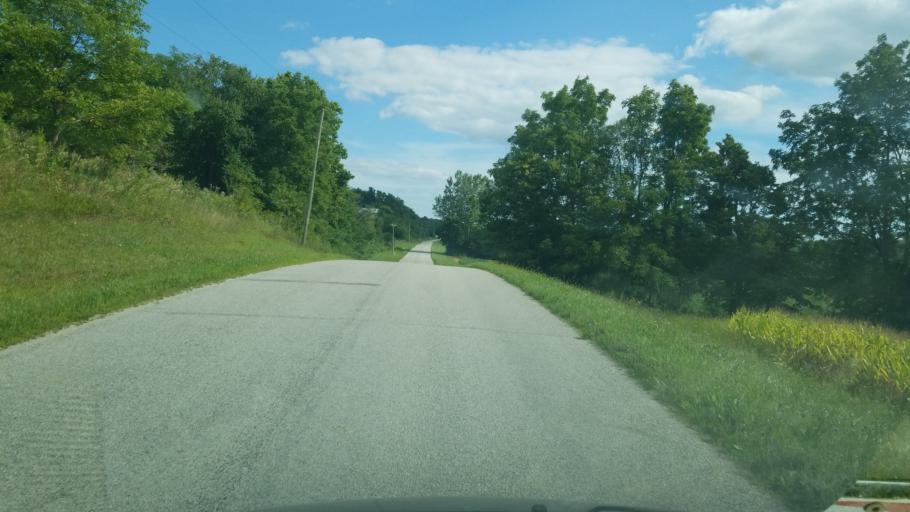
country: US
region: Ohio
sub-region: Champaign County
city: Saint Paris
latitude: 40.1703
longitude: -83.9348
